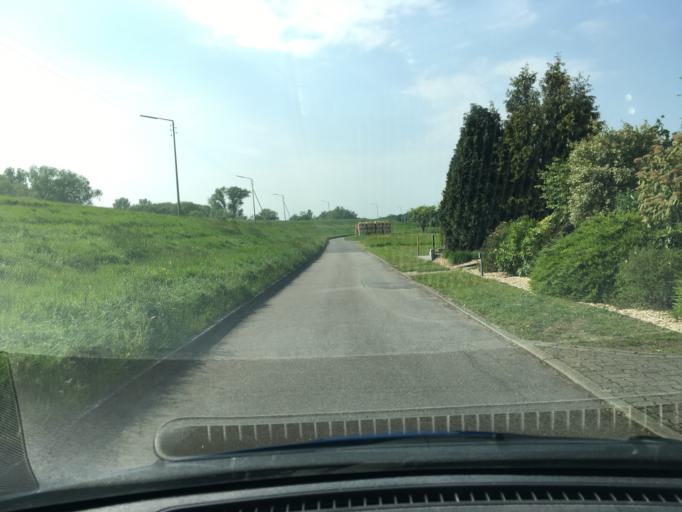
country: DE
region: Hamburg
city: Rothenburgsort
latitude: 53.4676
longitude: 10.0538
